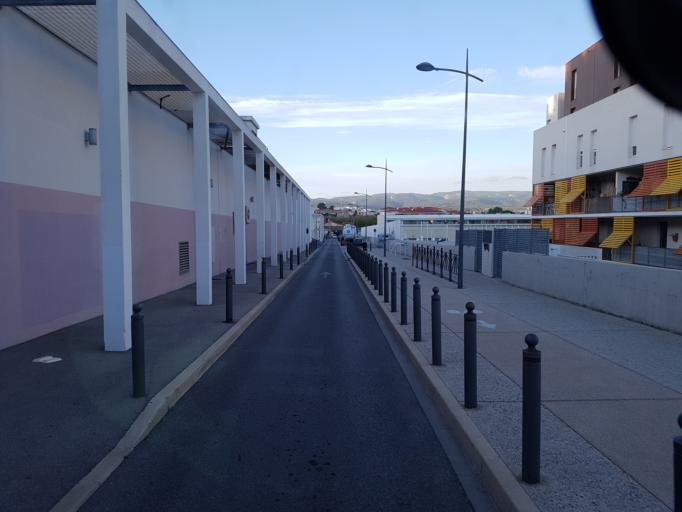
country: FR
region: Provence-Alpes-Cote d'Azur
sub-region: Departement des Bouches-du-Rhone
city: La Ciotat
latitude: 43.1715
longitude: 5.6030
